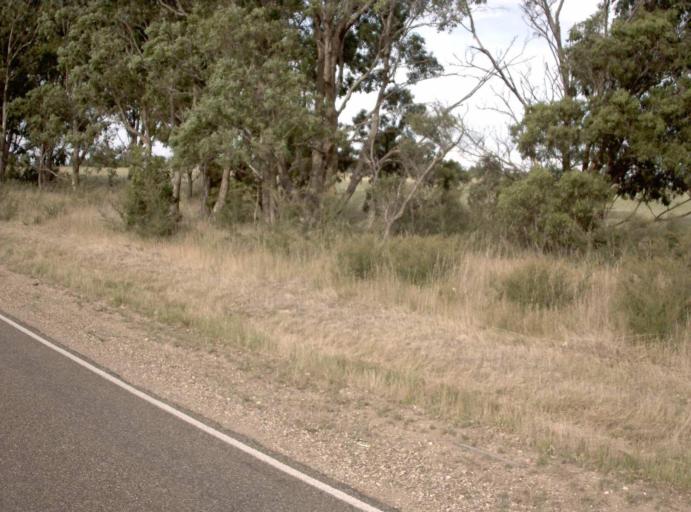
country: AU
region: Victoria
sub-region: Wellington
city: Heyfield
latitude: -38.0432
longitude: 146.6653
